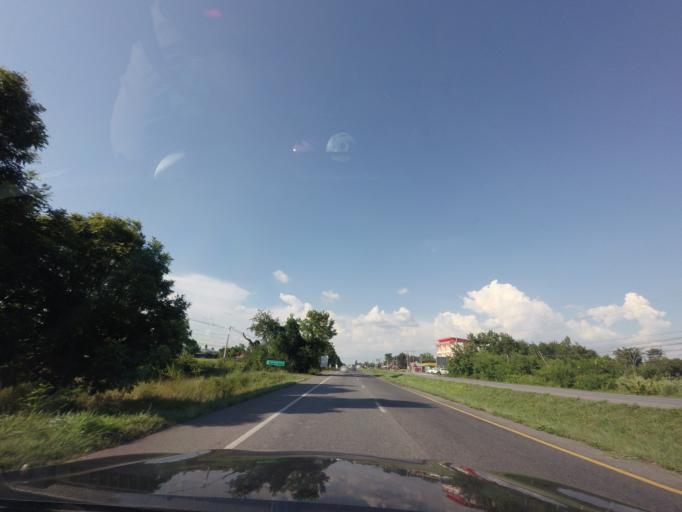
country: TH
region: Khon Kaen
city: Non Sila
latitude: 15.9968
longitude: 102.7006
